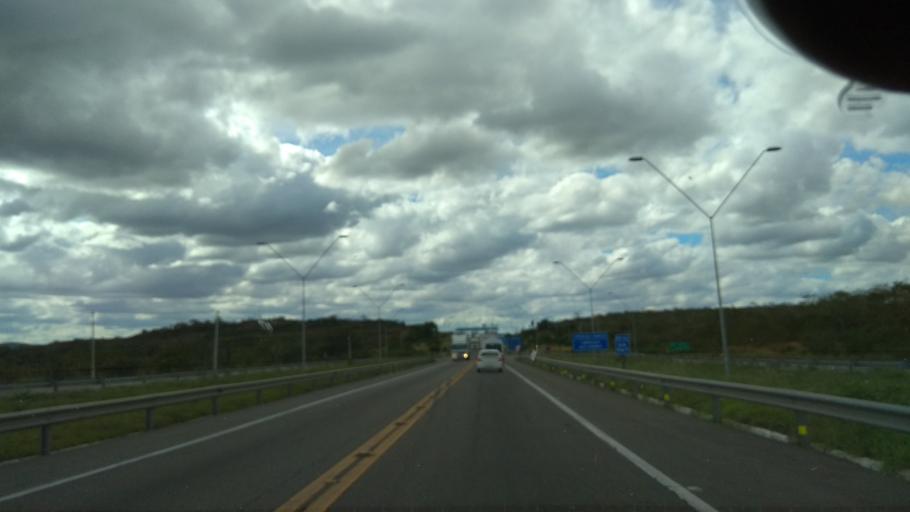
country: BR
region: Bahia
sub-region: Santa Ines
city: Santa Ines
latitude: -13.0146
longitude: -39.9586
